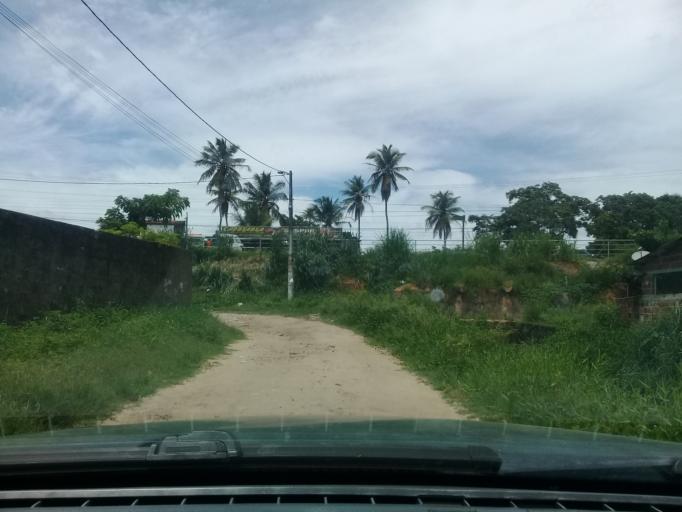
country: BR
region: Pernambuco
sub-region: Igarassu
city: Igarassu
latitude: -7.8456
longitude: -34.9087
